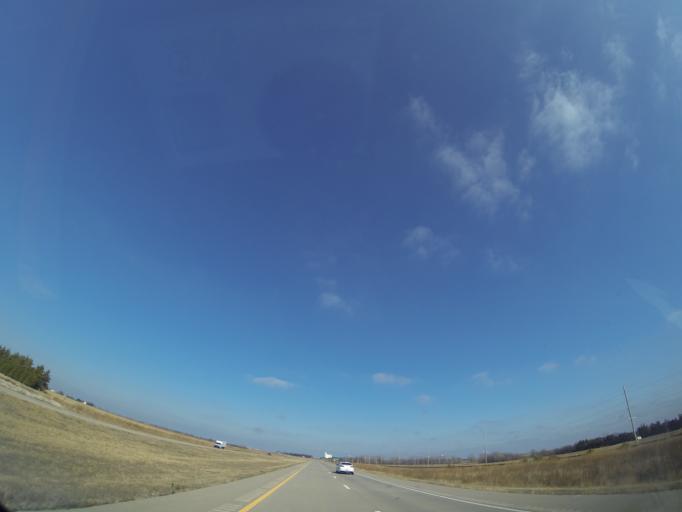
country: US
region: Kansas
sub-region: McPherson County
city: Inman
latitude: 38.2142
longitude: -97.7916
